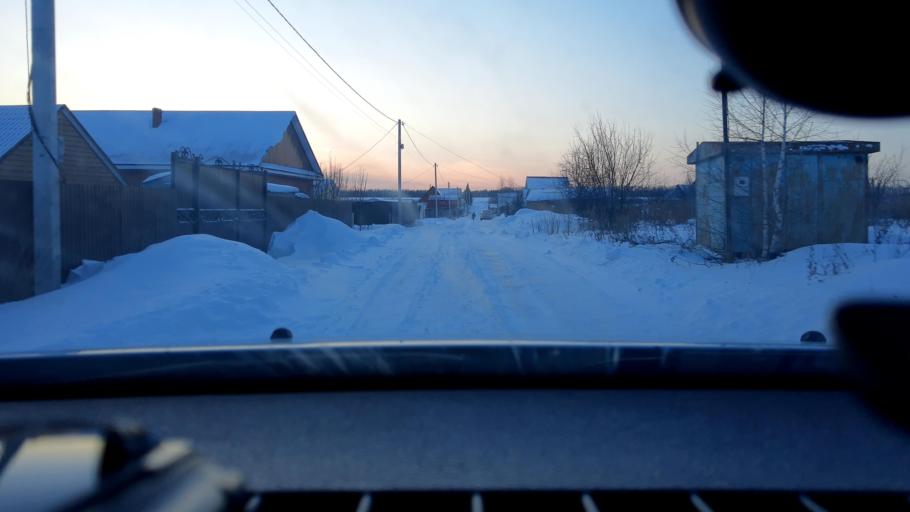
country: RU
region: Bashkortostan
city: Iglino
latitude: 54.8622
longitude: 56.4774
